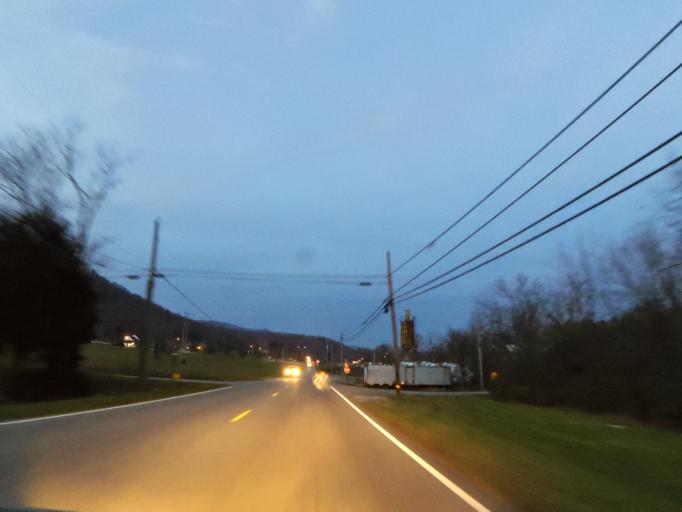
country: US
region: Tennessee
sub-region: Roane County
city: Oliver Springs
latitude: 36.0296
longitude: -84.3668
